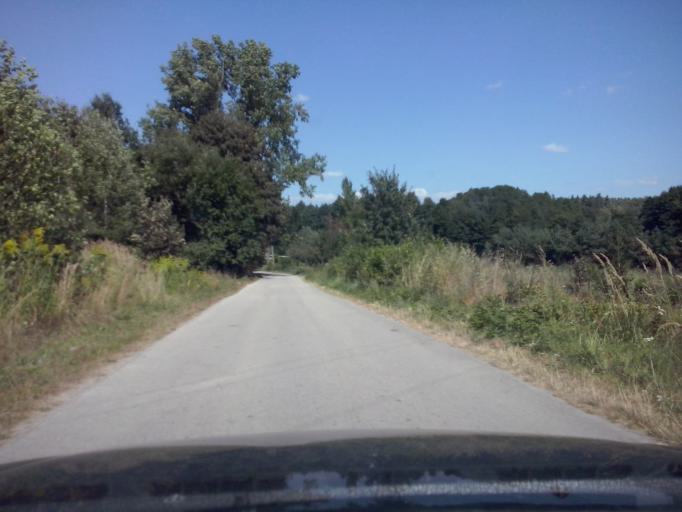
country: PL
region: Swietokrzyskie
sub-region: Powiat buski
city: Gnojno
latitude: 50.6033
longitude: 20.8918
